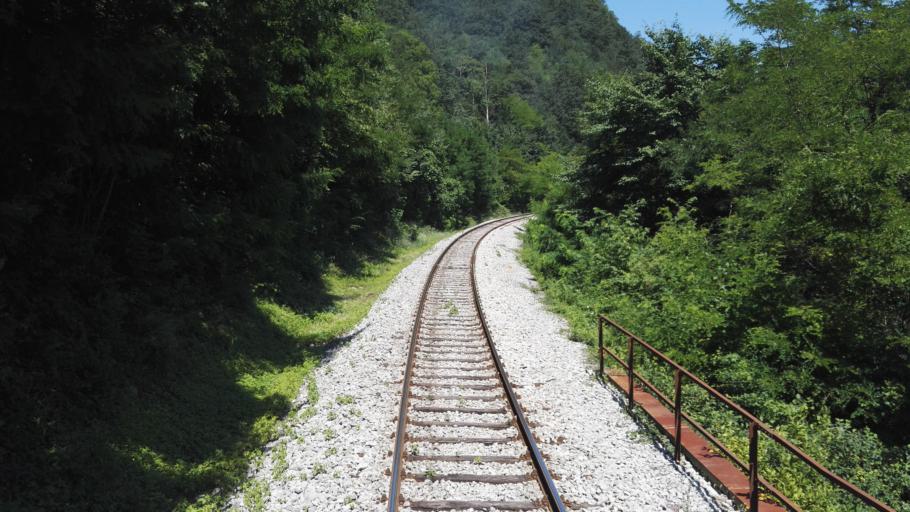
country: SI
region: Kanal
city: Deskle
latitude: 46.0175
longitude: 13.6057
